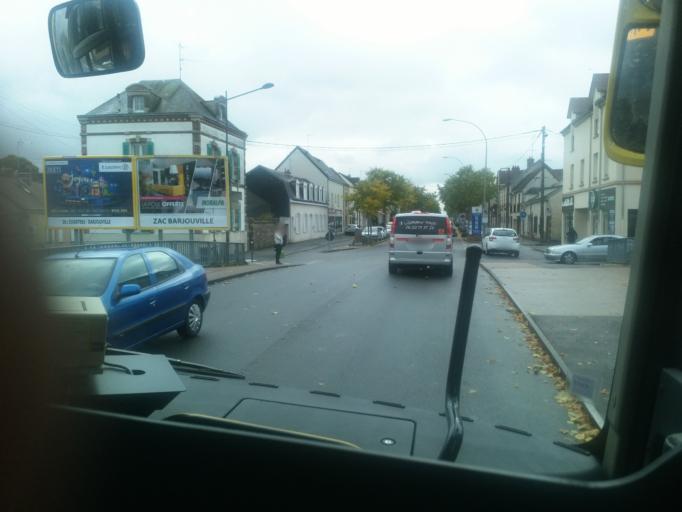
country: FR
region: Centre
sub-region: Departement d'Eure-et-Loir
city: Luisant
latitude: 48.4367
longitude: 1.4798
